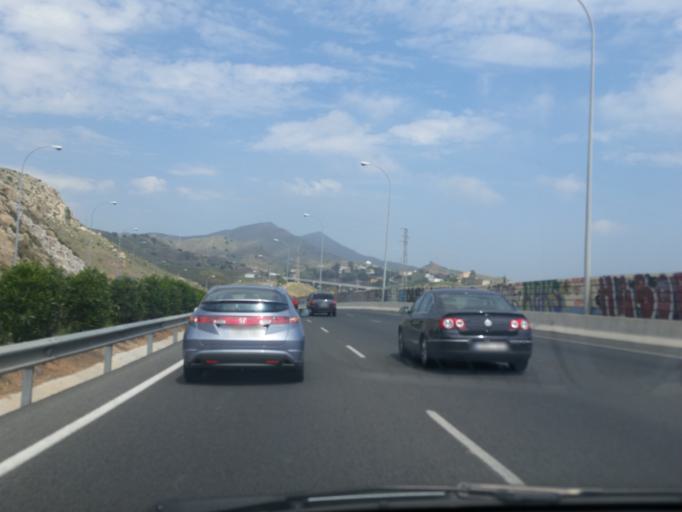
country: ES
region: Andalusia
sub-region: Provincia de Malaga
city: Malaga
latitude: 36.7346
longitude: -4.4540
